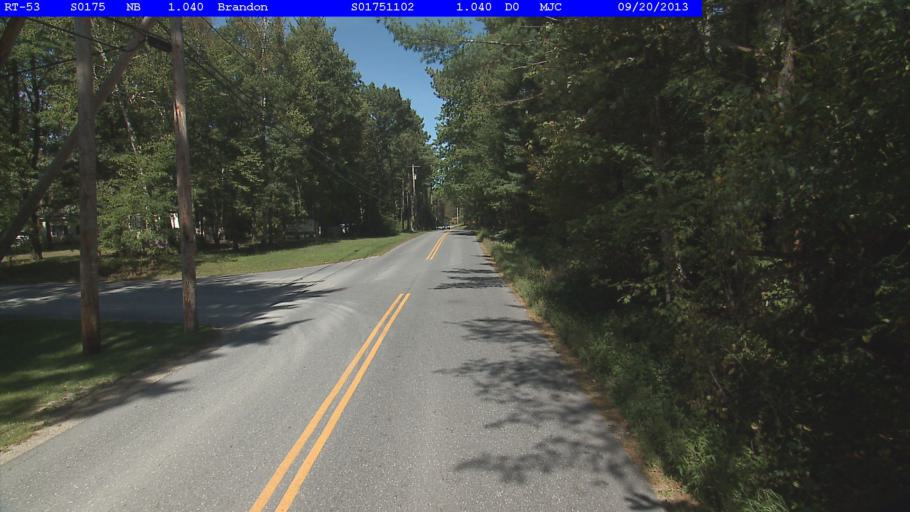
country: US
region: Vermont
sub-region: Rutland County
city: Brandon
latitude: 43.8417
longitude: -73.0566
